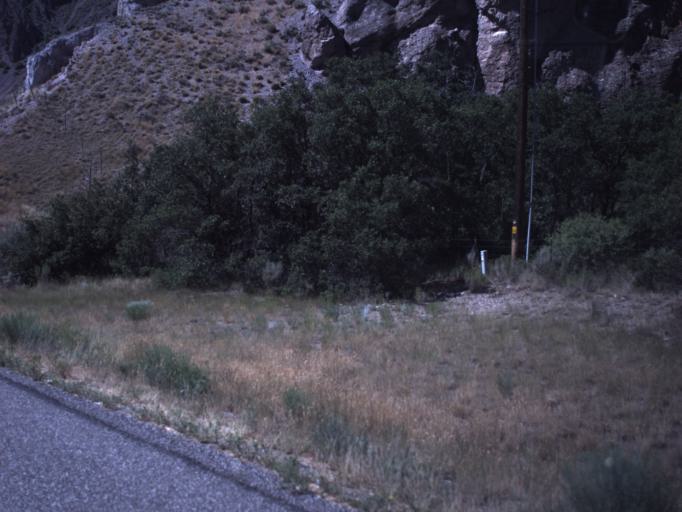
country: US
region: Utah
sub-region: Sevier County
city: Monroe
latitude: 38.5026
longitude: -112.2581
